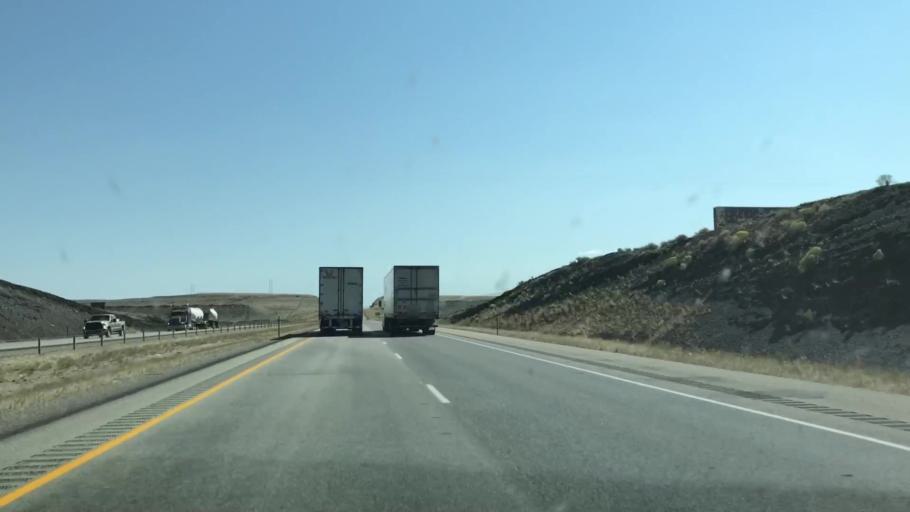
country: US
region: Wyoming
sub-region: Carbon County
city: Rawlins
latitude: 41.7832
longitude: -107.1617
